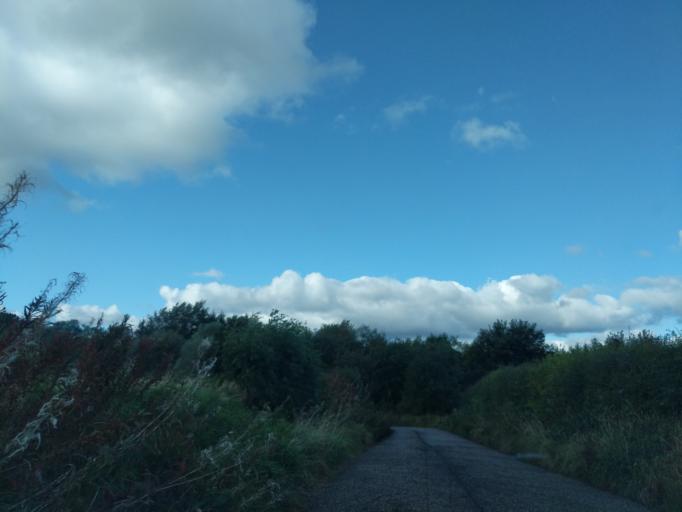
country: GB
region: Scotland
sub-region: Edinburgh
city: Currie
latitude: 55.9212
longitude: -3.3273
